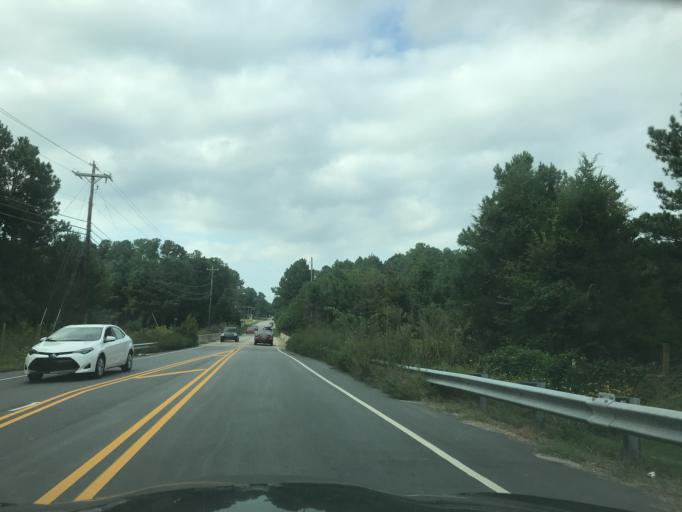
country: US
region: North Carolina
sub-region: Durham County
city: Durham
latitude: 35.9080
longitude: -78.9163
